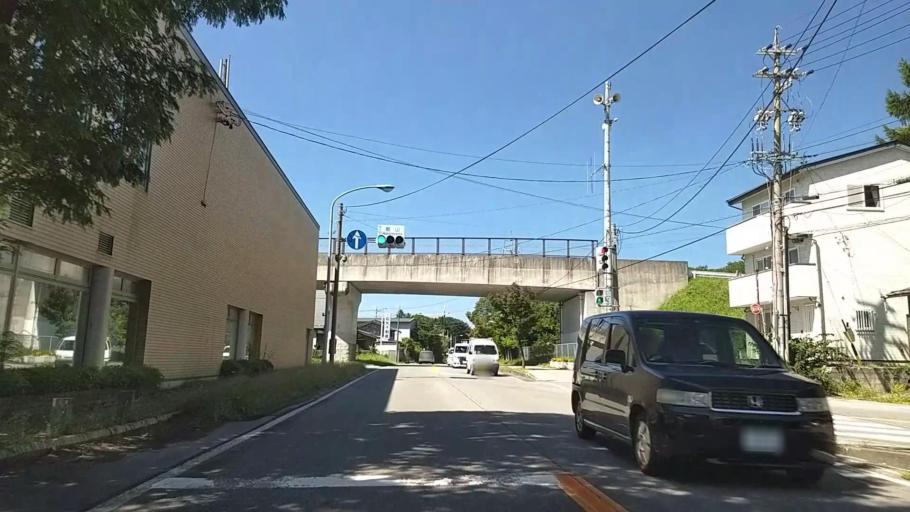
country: JP
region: Nagano
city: Komoro
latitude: 36.3439
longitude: 138.6085
